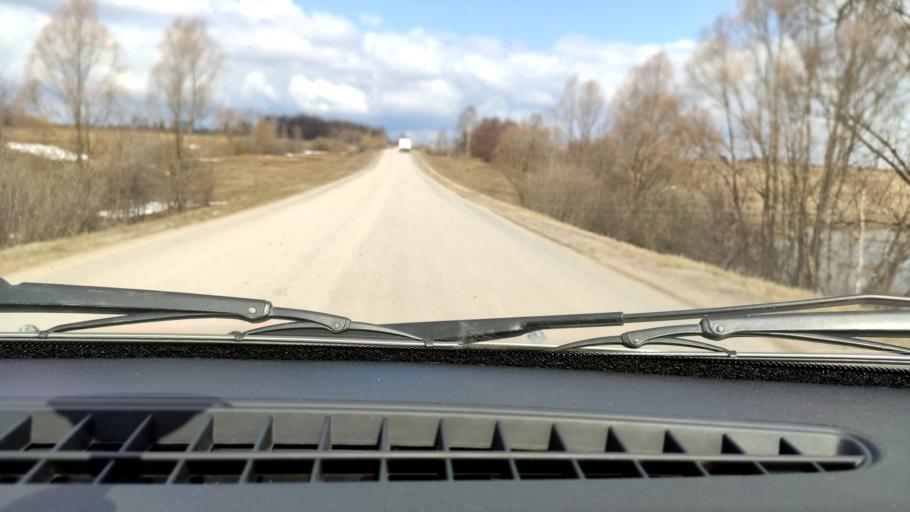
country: RU
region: Bashkortostan
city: Kudeyevskiy
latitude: 54.8185
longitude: 56.7937
